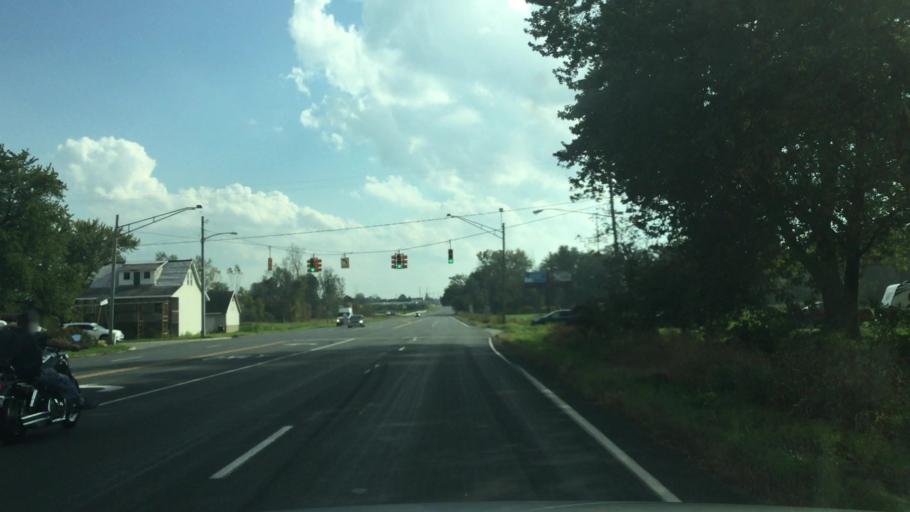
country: US
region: Michigan
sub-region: Kalamazoo County
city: Eastwood
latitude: 42.2781
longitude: -85.5308
